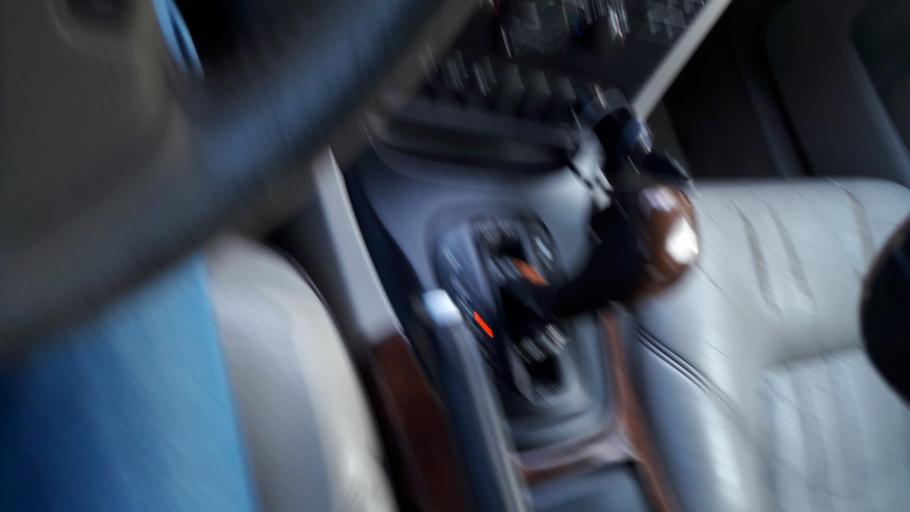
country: BG
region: Razgrad
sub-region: Obshtina Razgrad
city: Razgrad
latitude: 43.5397
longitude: 26.5168
